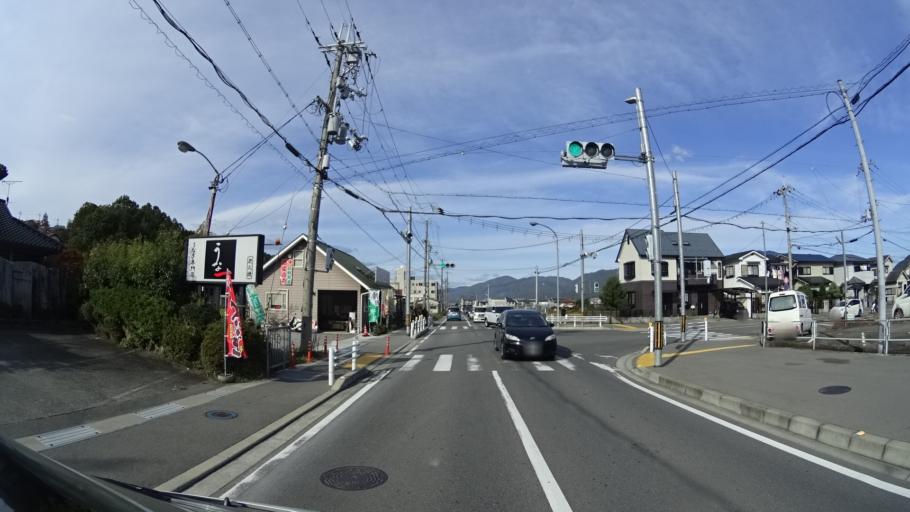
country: JP
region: Kyoto
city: Kameoka
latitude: 35.0005
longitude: 135.5781
